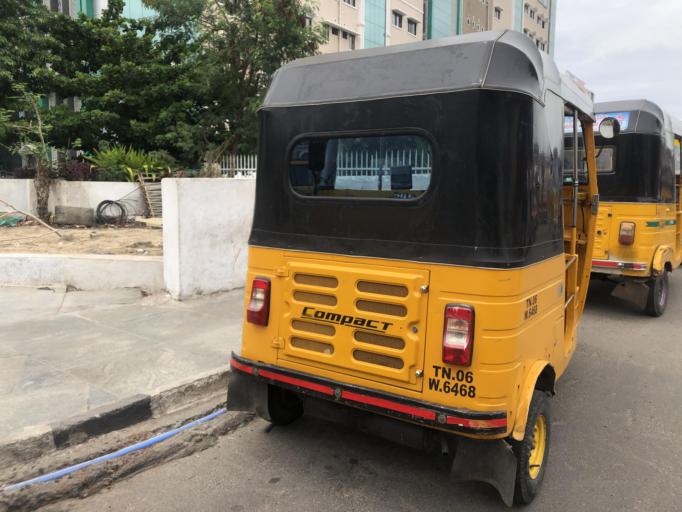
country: IN
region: Tamil Nadu
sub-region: Chennai
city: Chennai
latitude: 13.0815
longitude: 80.2753
